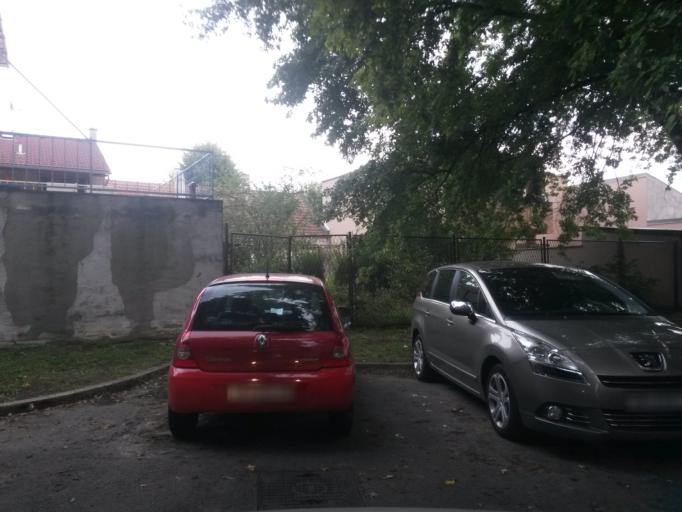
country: HR
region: Osjecko-Baranjska
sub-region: Grad Osijek
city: Osijek
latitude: 45.5502
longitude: 18.6846
